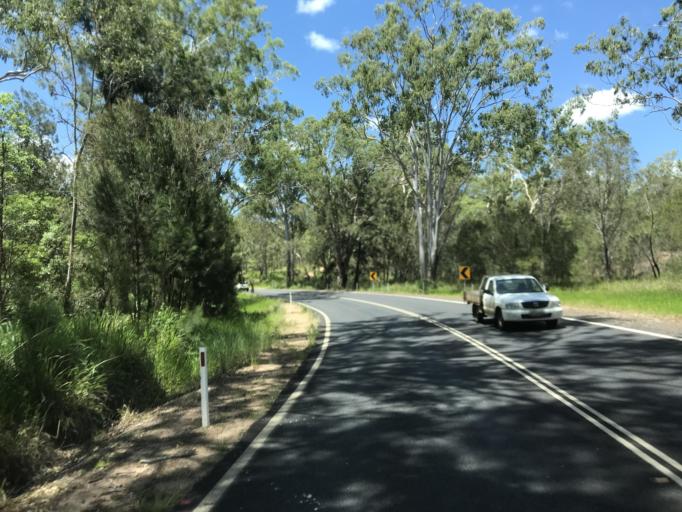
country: AU
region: Queensland
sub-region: Tablelands
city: Atherton
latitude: -17.4032
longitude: 145.3901
